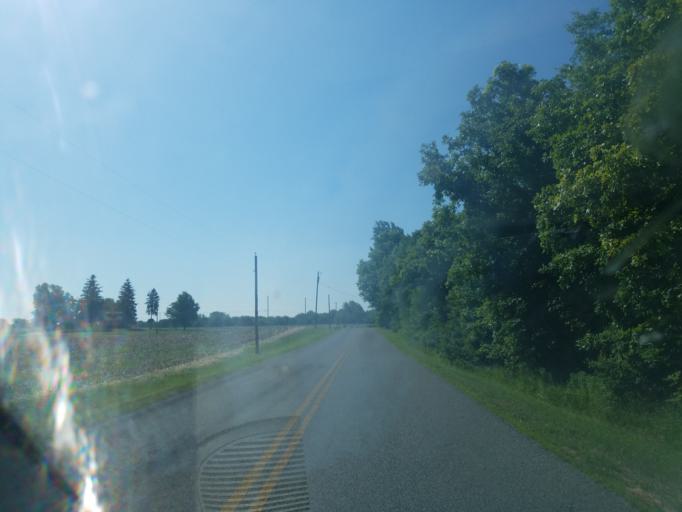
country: US
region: Ohio
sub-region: Logan County
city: Northwood
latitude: 40.4268
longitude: -83.7057
